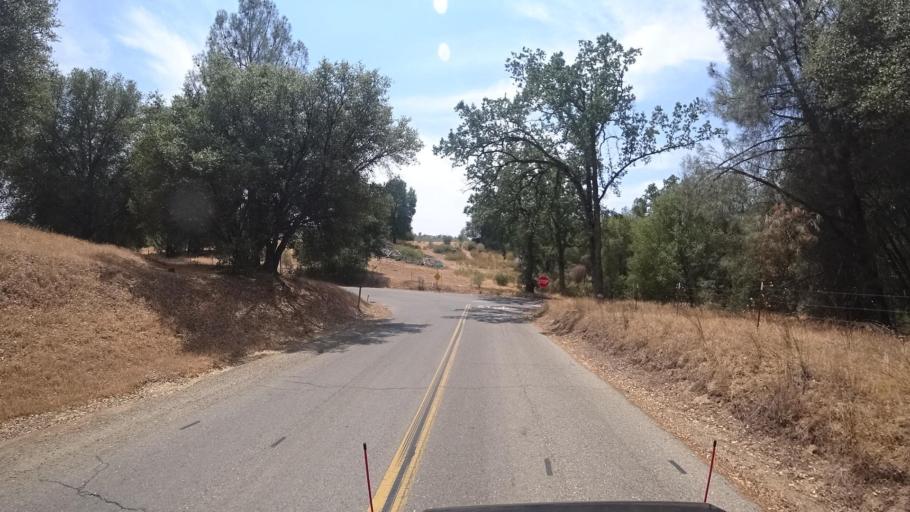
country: US
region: California
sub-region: Mariposa County
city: Mariposa
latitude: 37.4167
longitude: -119.8624
